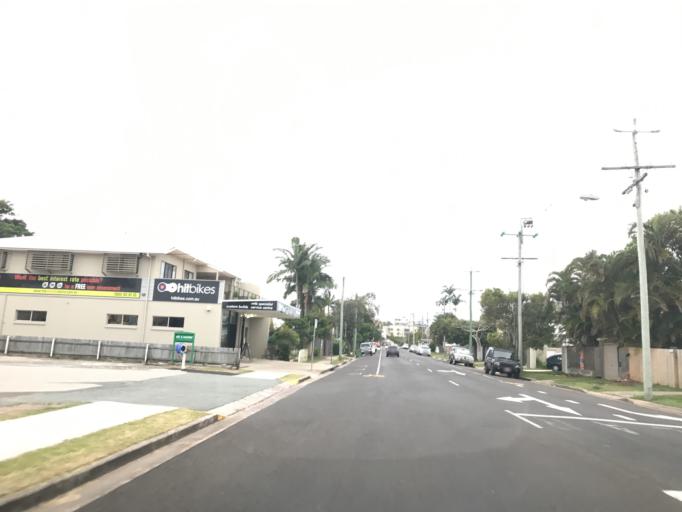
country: AU
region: Queensland
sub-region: Sunshine Coast
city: Dicky Beach
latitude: -26.7899
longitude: 153.1383
